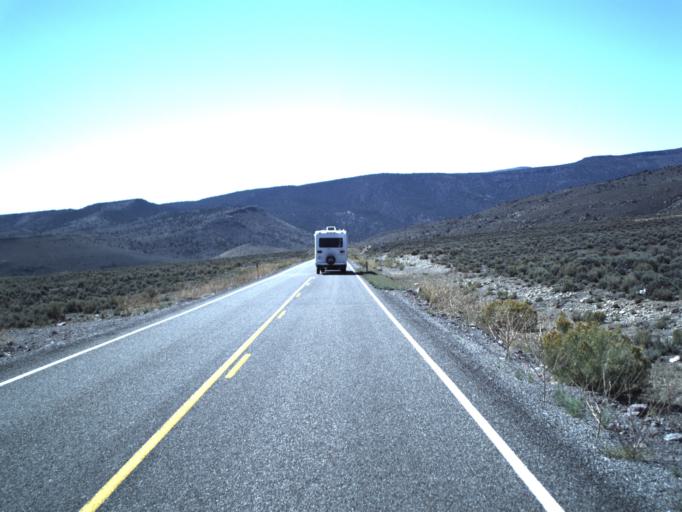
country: US
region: Utah
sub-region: Piute County
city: Junction
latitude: 38.1816
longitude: -112.0179
